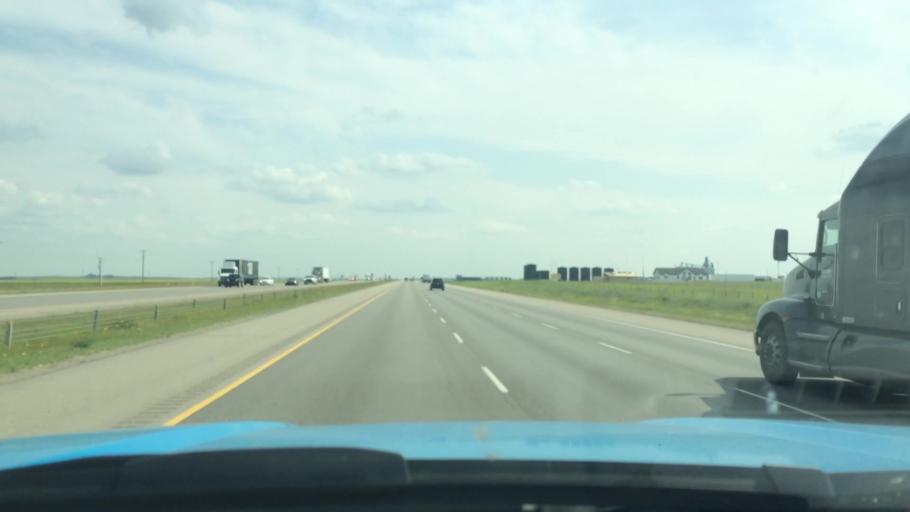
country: CA
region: Alberta
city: Crossfield
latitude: 51.5064
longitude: -114.0253
